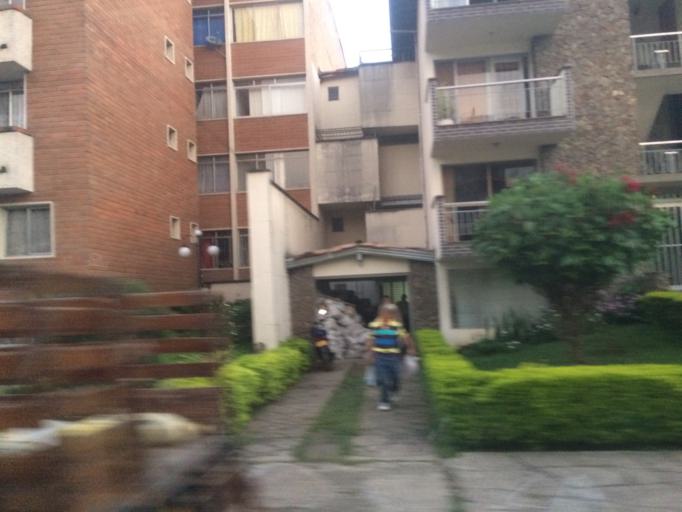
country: CO
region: Antioquia
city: Medellin
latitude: 6.2510
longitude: -75.5866
